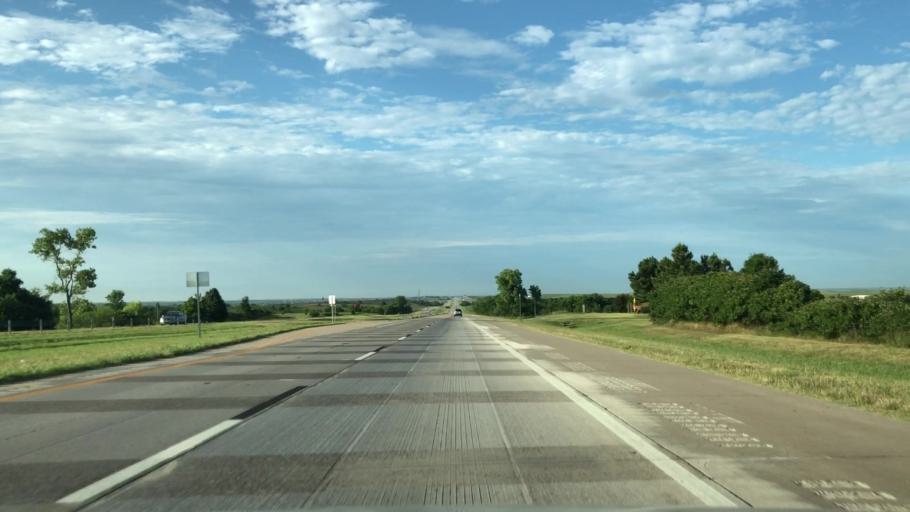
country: US
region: Oklahoma
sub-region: Osage County
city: Skiatook
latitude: 36.4173
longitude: -95.9207
